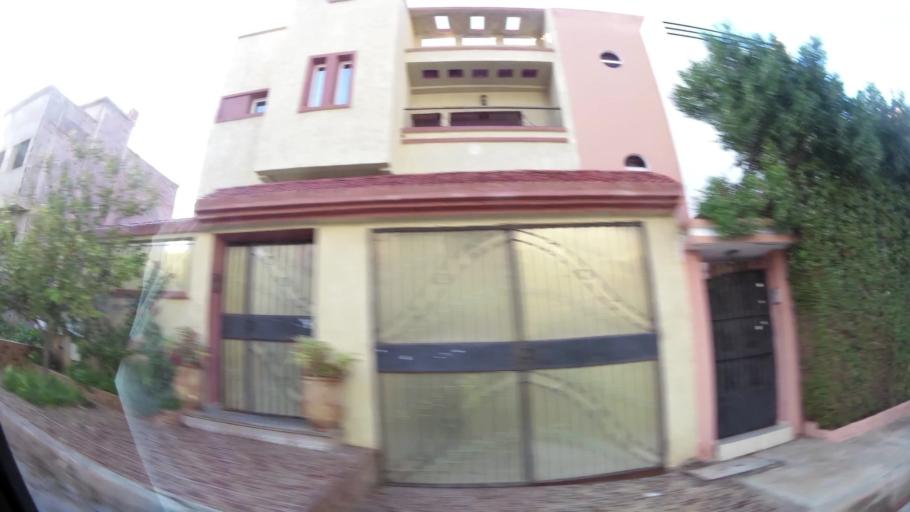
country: MA
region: Chaouia-Ouardigha
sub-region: Settat Province
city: Settat
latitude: 33.0096
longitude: -7.6126
